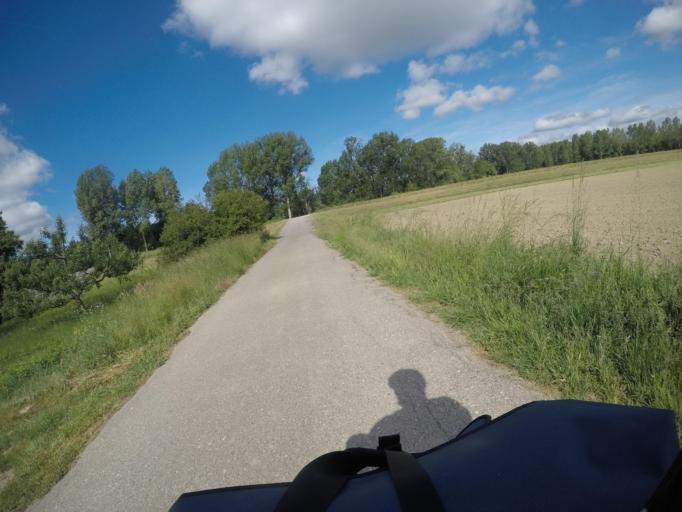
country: DE
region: Baden-Wuerttemberg
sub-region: Karlsruhe Region
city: Au am Rhein
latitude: 48.9388
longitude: 8.2007
